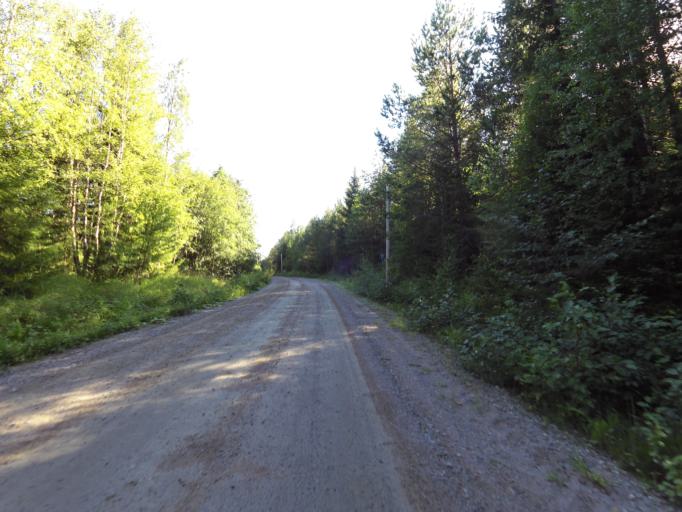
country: SE
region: Gaevleborg
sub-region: Hofors Kommun
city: Hofors
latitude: 60.6310
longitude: 16.2790
